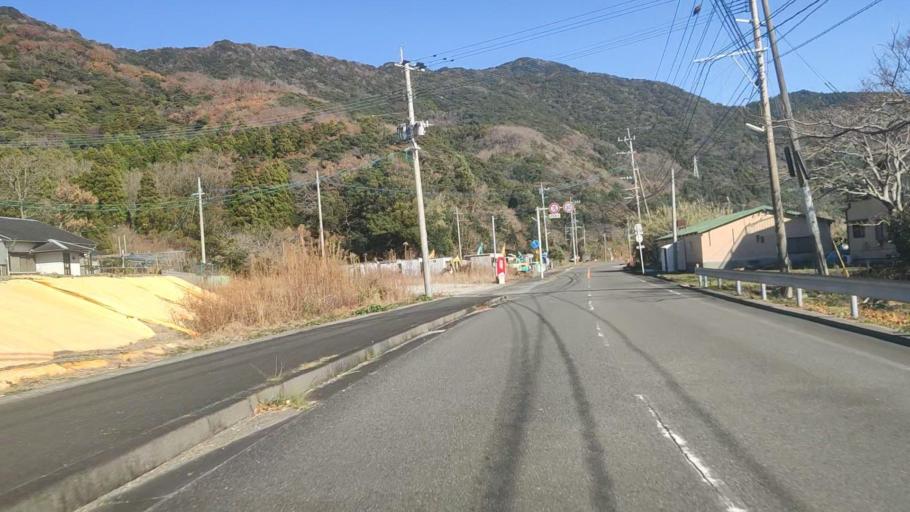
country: JP
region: Oita
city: Saiki
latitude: 32.8055
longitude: 131.9454
